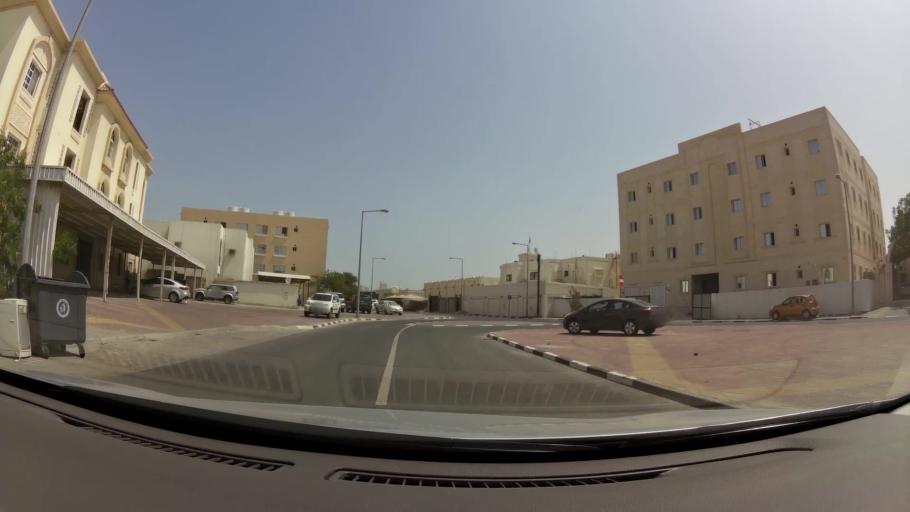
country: QA
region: Baladiyat ad Dawhah
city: Doha
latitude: 25.3217
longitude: 51.4846
